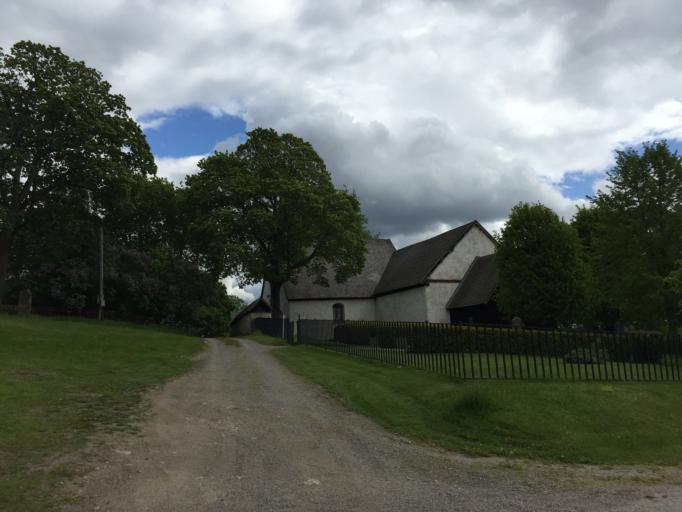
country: SE
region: OEstergoetland
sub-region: Finspangs Kommun
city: Finspang
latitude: 58.6754
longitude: 15.8431
